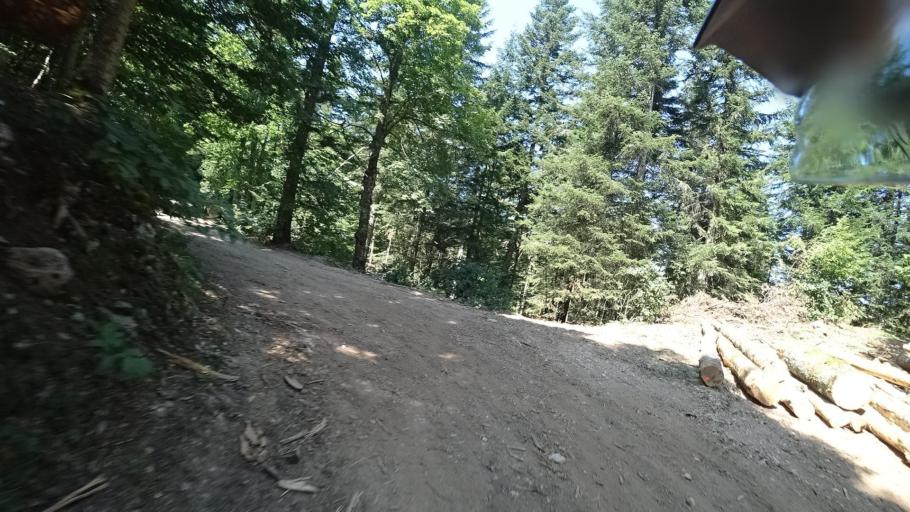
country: HR
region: Licko-Senjska
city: Popovaca
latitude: 44.5766
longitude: 15.1971
